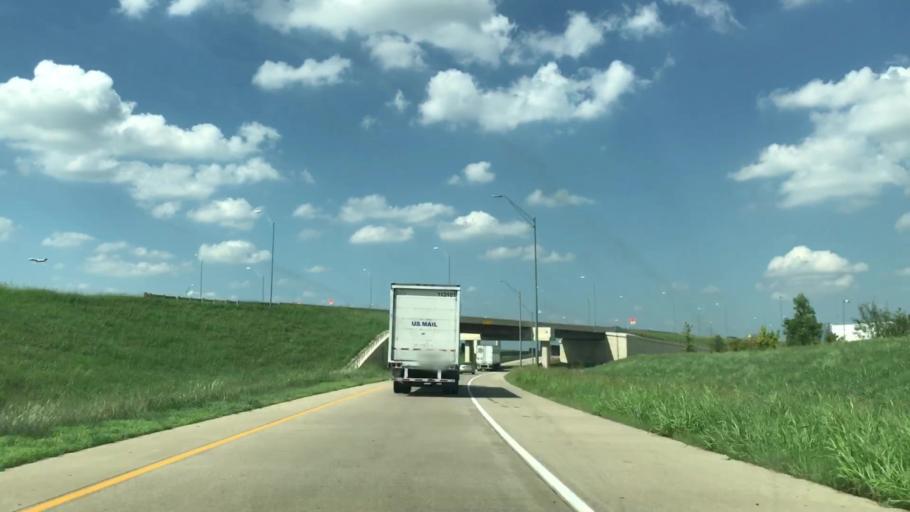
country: US
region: Texas
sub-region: Dallas County
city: Coppell
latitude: 32.9349
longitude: -97.0383
